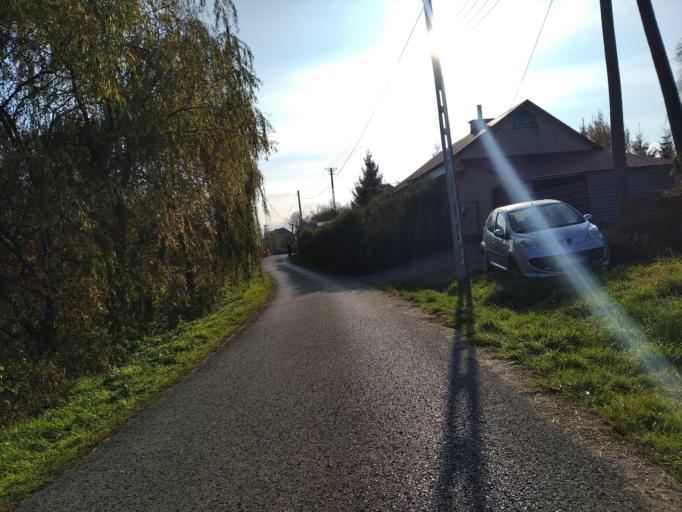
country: PL
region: Subcarpathian Voivodeship
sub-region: Powiat strzyzowski
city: Babica
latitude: 49.9050
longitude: 21.8513
